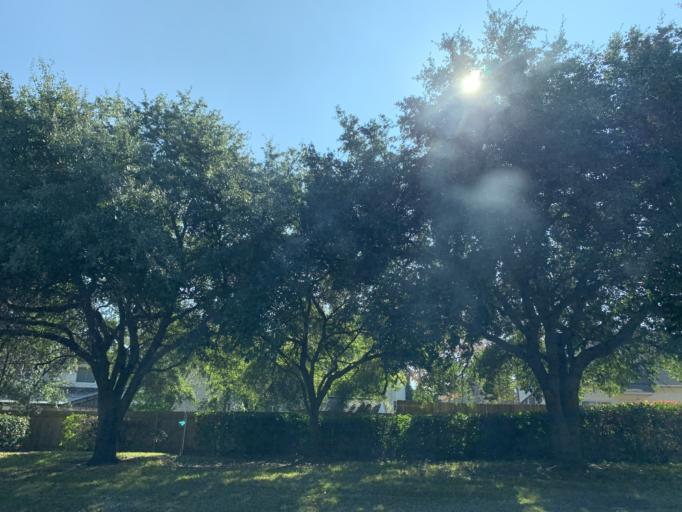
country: US
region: Texas
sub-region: Williamson County
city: Round Rock
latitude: 30.4996
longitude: -97.6391
